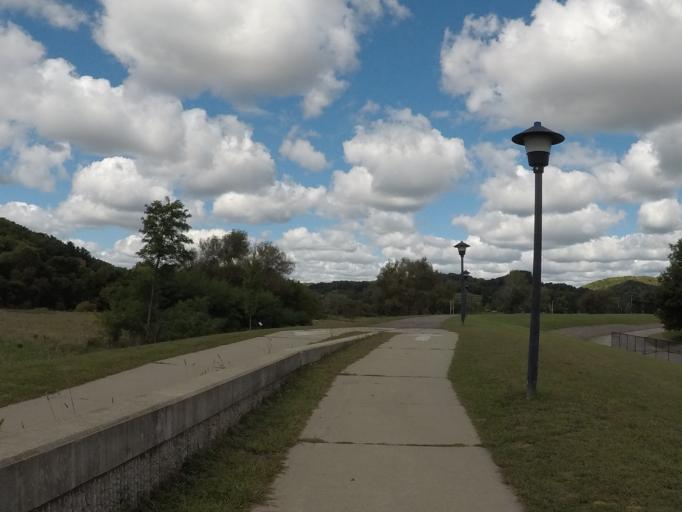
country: US
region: Wisconsin
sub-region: Richland County
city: Richland Center
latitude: 43.3394
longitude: -90.3909
